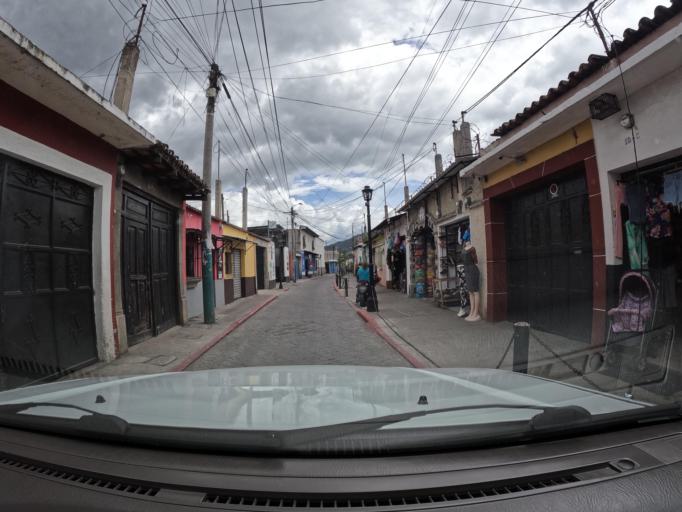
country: GT
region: Sacatepequez
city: Jocotenango
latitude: 14.5771
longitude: -90.7405
